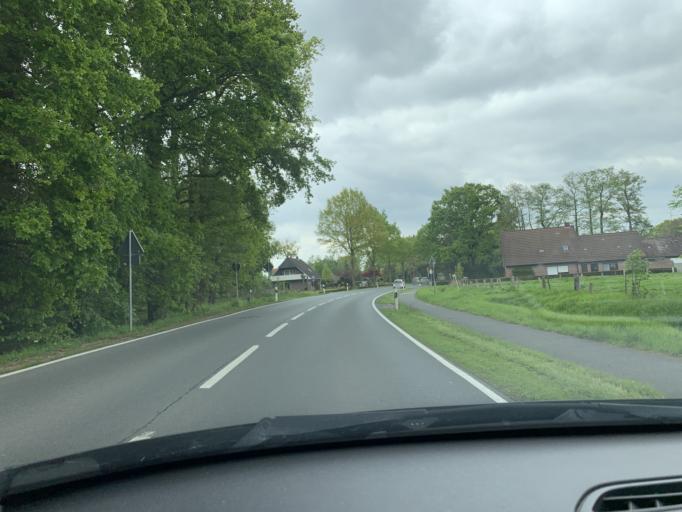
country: DE
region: Lower Saxony
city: Bad Zwischenahn
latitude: 53.2173
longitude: 8.0094
